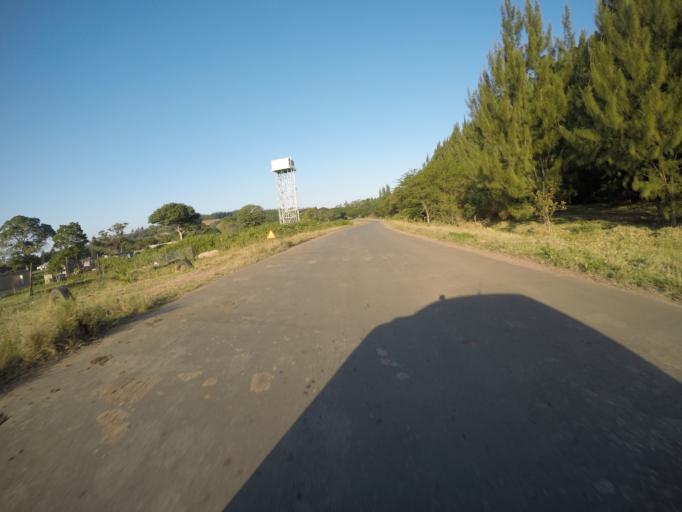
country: ZA
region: KwaZulu-Natal
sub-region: uThungulu District Municipality
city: KwaMbonambi
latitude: -28.7074
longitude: 32.1810
